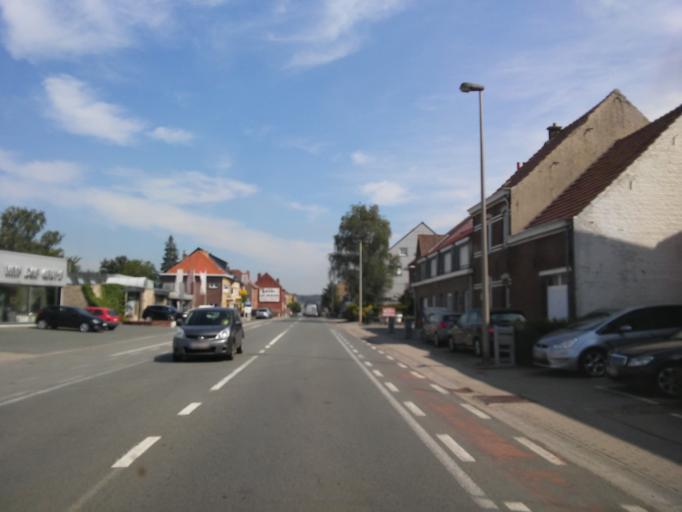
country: BE
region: Flanders
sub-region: Provincie Vlaams-Brabant
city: Ternat
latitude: 50.8706
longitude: 4.1613
